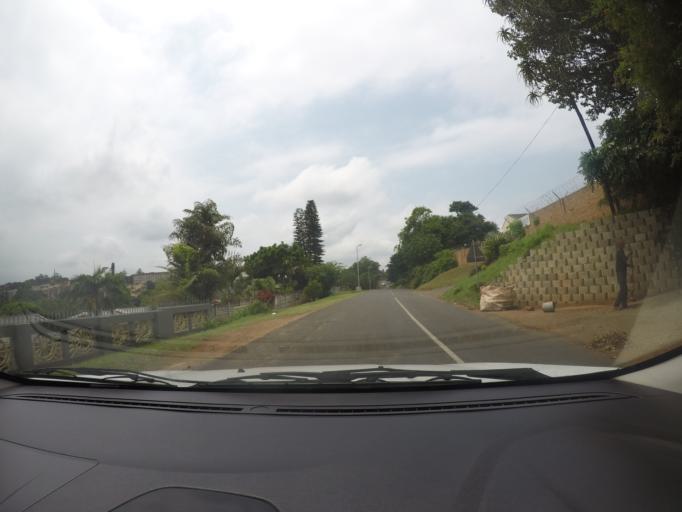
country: ZA
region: KwaZulu-Natal
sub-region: uThungulu District Municipality
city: Empangeni
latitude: -28.7516
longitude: 31.8898
